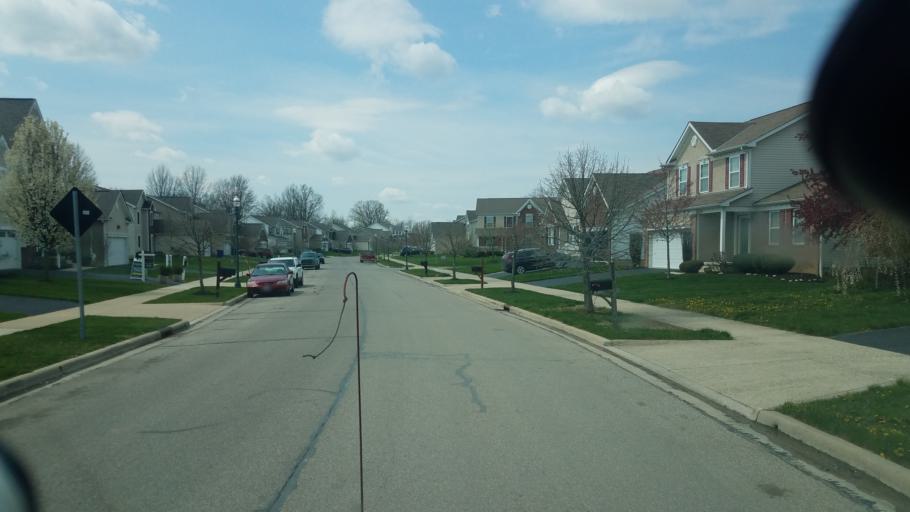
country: US
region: Ohio
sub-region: Delaware County
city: Delaware
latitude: 40.2921
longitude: -83.0912
